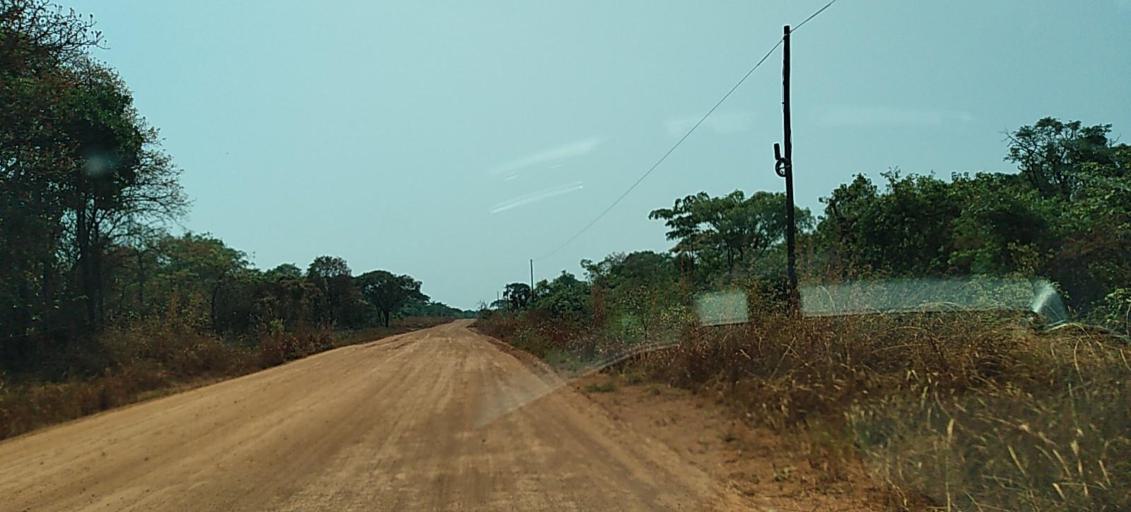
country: ZM
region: North-Western
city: Kansanshi
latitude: -11.9925
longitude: 26.6197
